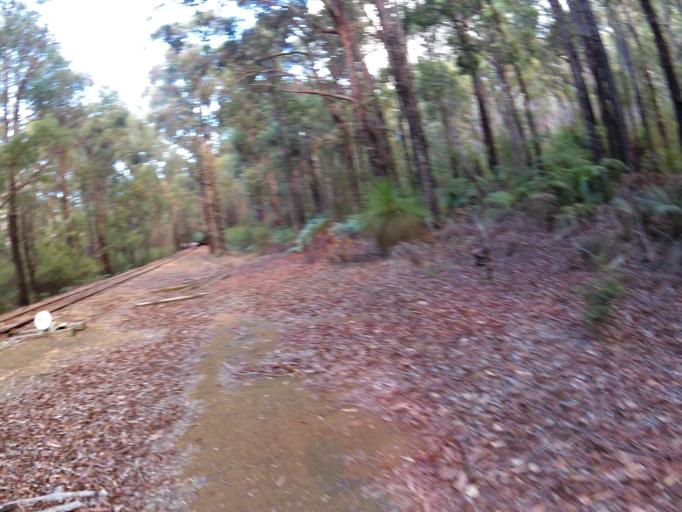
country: AU
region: Western Australia
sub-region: Waroona
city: Waroona
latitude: -32.7387
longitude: 116.1399
